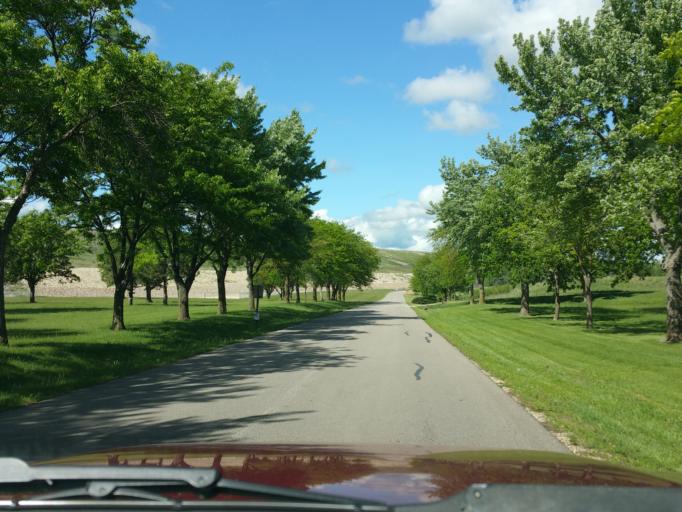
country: US
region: Kansas
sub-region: Riley County
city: Manhattan
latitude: 39.2511
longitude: -96.5971
